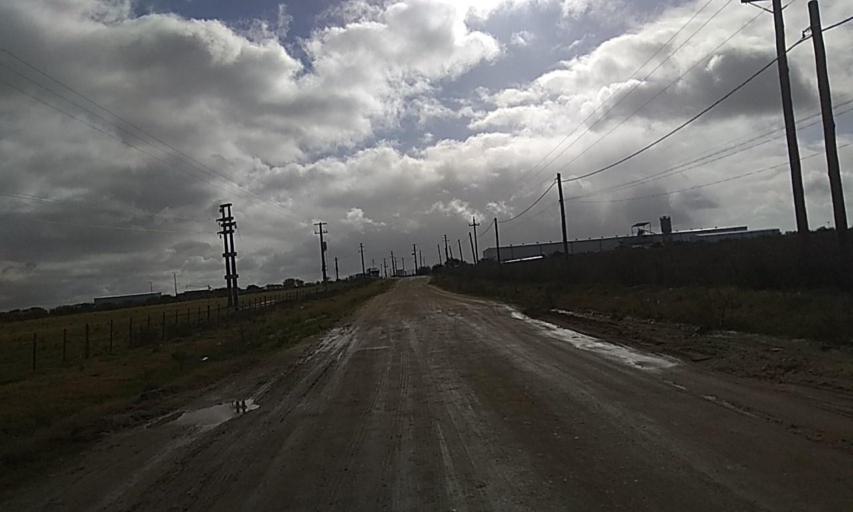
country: UY
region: Florida
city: Florida
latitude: -34.0940
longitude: -56.1895
